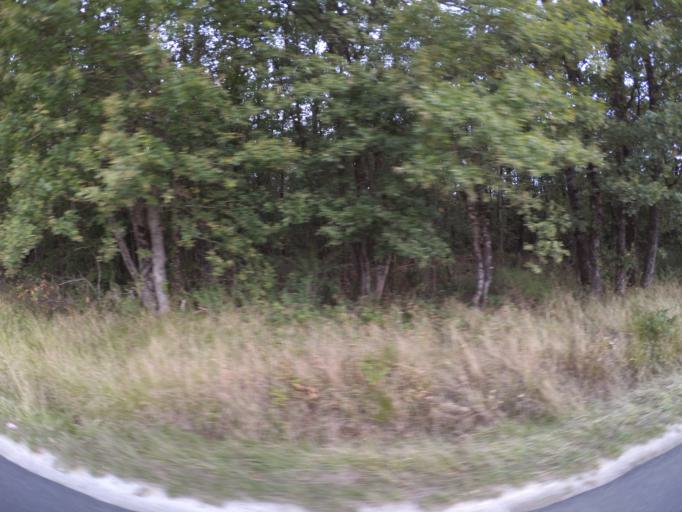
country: FR
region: Centre
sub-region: Departement d'Indre-et-Loire
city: Nazelles-Negron
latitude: 47.4802
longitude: 0.9508
